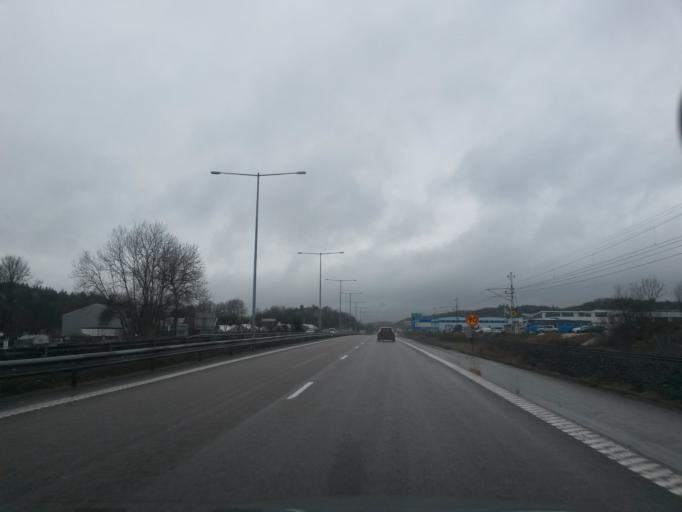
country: SE
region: Vaestra Goetaland
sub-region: Uddevalla Kommun
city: Uddevalla
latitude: 58.3516
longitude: 11.9769
